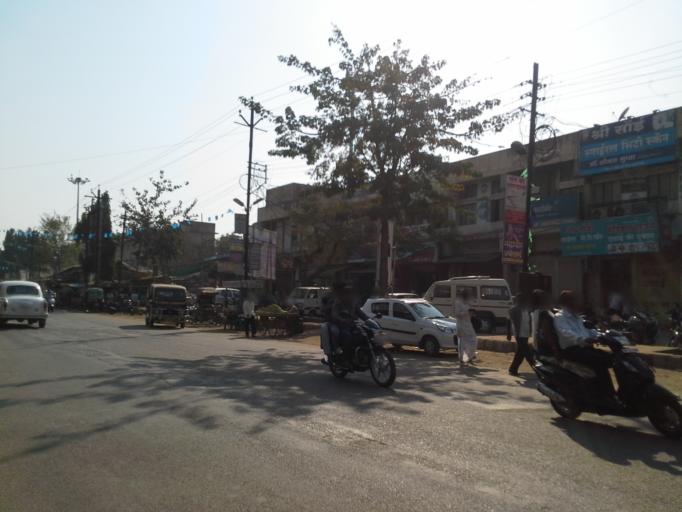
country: IN
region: Maharashtra
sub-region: Gondiya
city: Gondia
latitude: 21.4593
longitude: 80.1962
